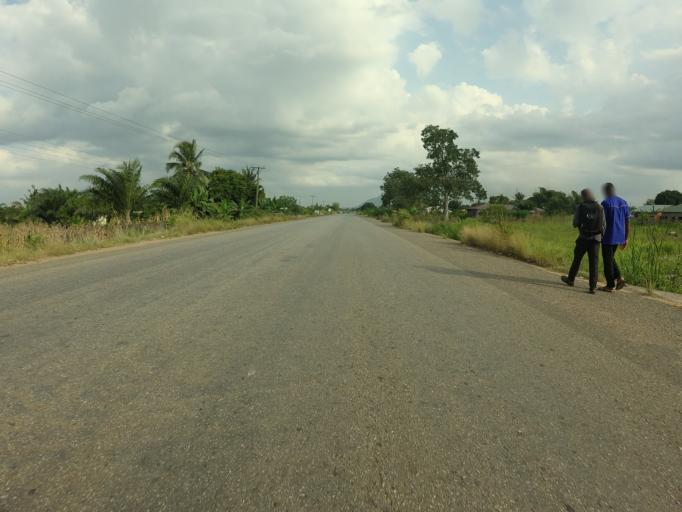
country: GH
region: Volta
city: Ho
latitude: 6.5822
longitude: 0.4811
